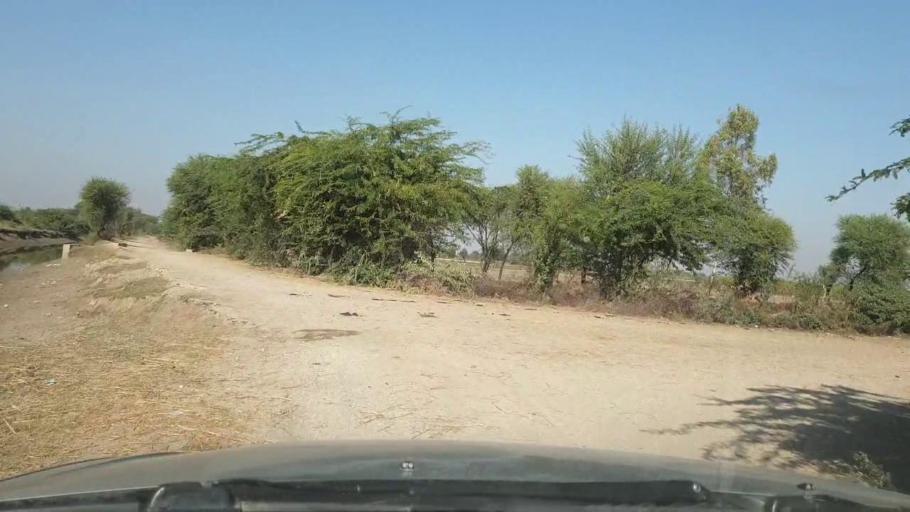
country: PK
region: Sindh
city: Kario
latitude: 24.9105
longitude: 68.5339
